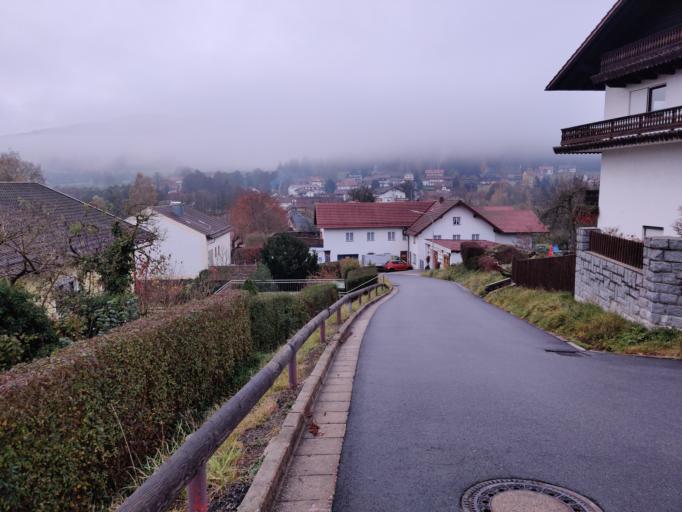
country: DE
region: Bavaria
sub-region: Upper Palatinate
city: Lam
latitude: 49.1943
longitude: 13.0536
